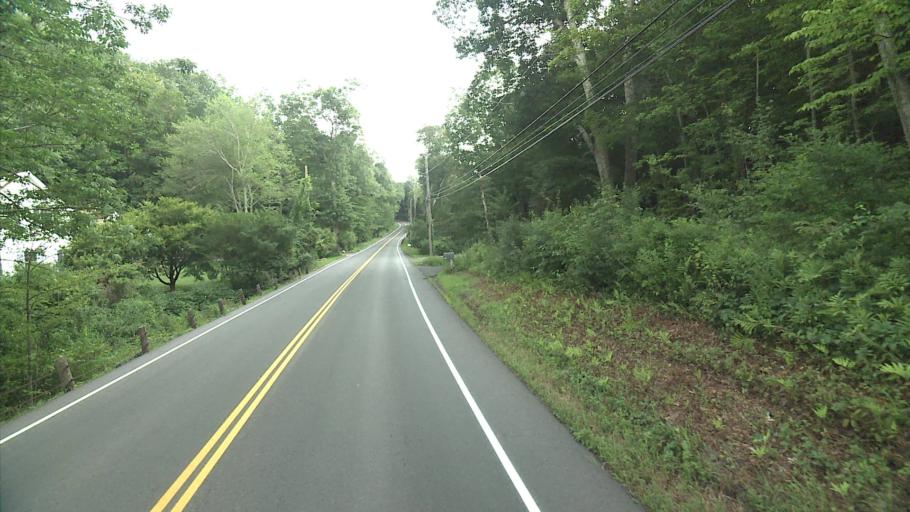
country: US
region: Connecticut
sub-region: New Haven County
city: Heritage Village
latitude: 41.5327
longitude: -73.2766
